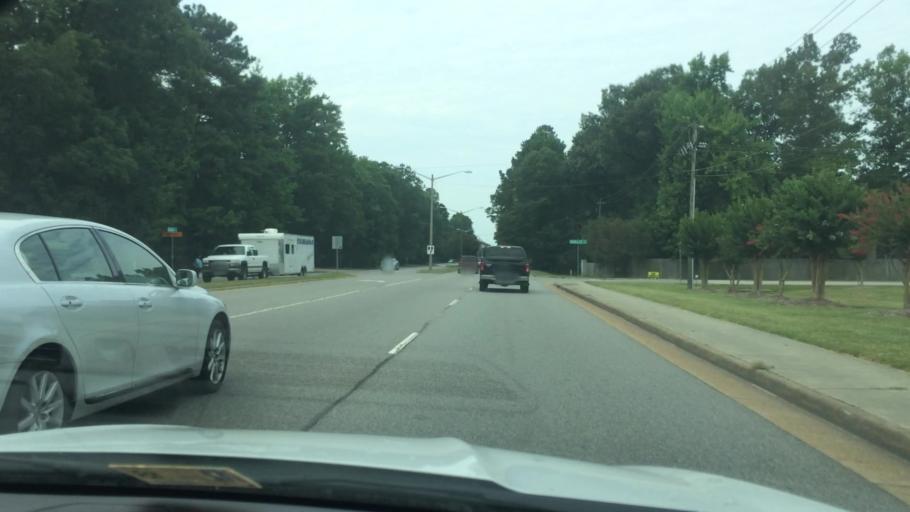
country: US
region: Virginia
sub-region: York County
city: Yorktown
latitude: 37.1514
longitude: -76.5085
